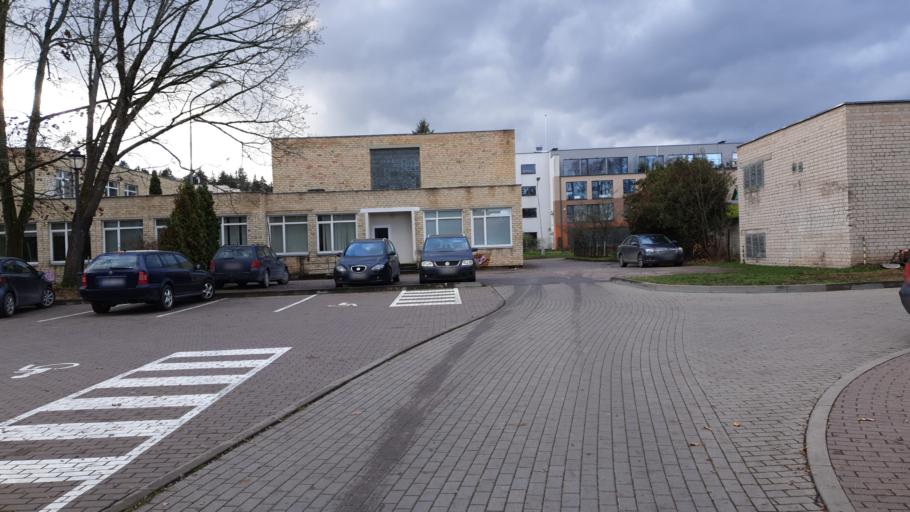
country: LT
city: Birstonas
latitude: 54.6023
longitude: 24.0335
